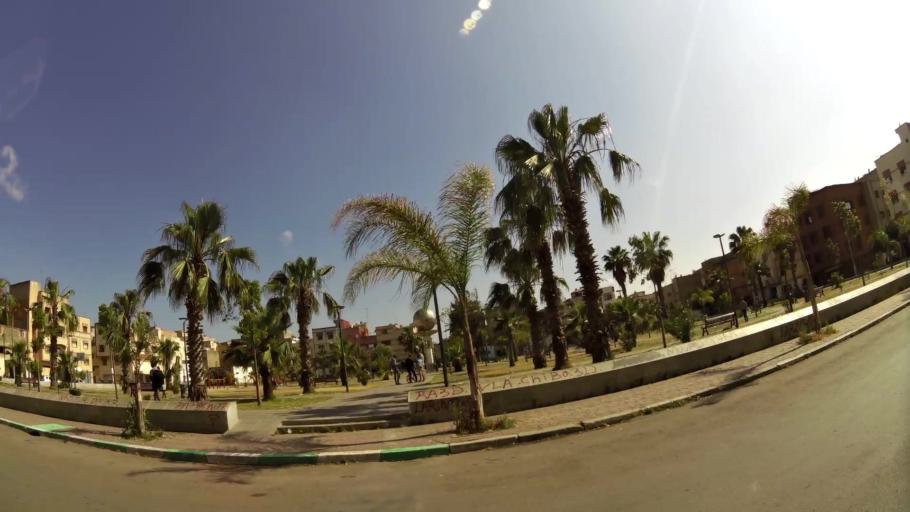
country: MA
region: Rabat-Sale-Zemmour-Zaer
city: Sale
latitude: 34.0429
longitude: -6.7823
